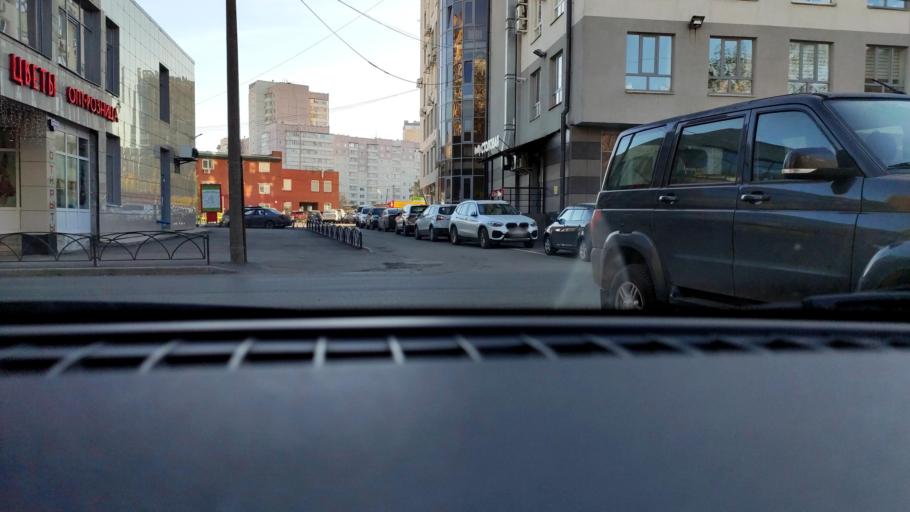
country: RU
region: Perm
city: Perm
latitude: 58.0020
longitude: 56.2950
